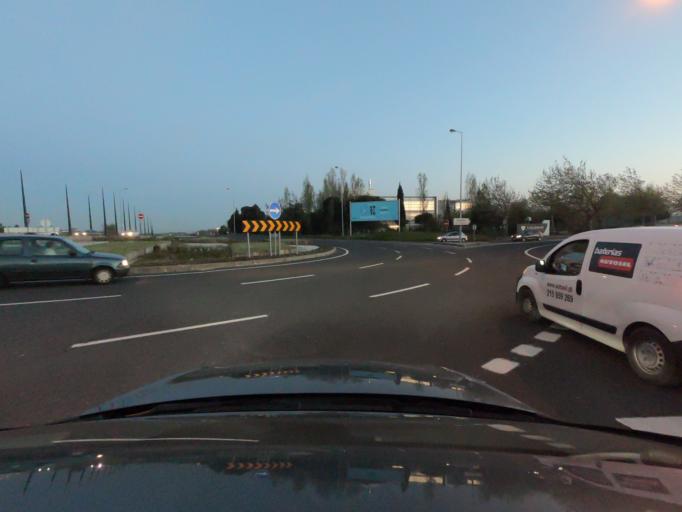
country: PT
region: Lisbon
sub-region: Sintra
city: Cacem
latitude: 38.7471
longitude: -9.3040
